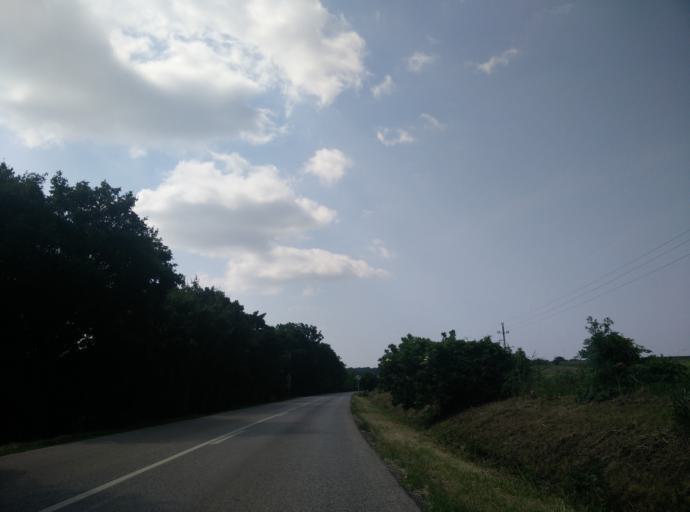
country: HU
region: Pest
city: Biatorbagy
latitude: 47.4746
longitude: 18.7950
